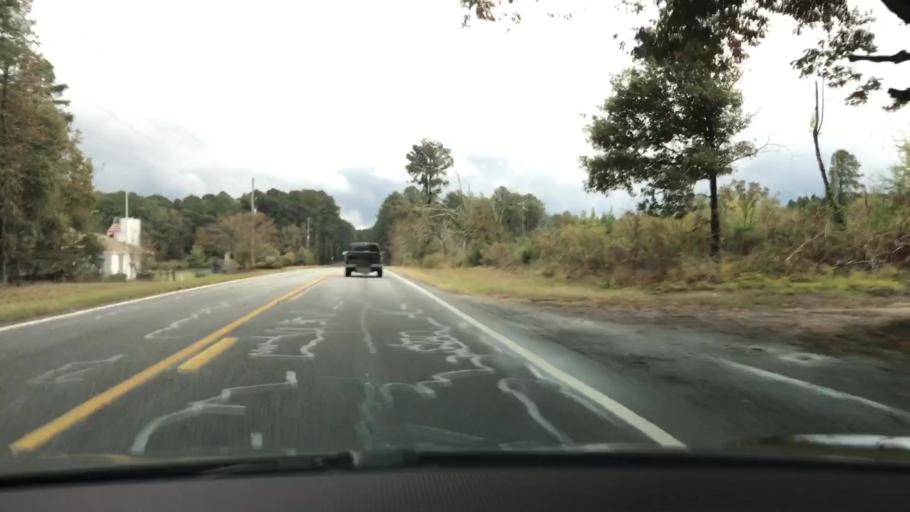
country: US
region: Georgia
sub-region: Oconee County
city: Watkinsville
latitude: 33.7870
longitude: -83.3174
